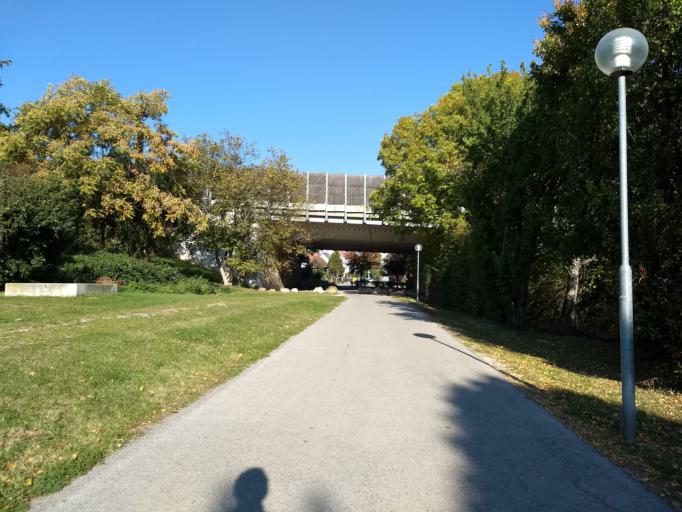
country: AT
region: Lower Austria
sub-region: Politischer Bezirk Modling
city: Brunn am Gebirge
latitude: 48.1106
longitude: 16.2737
